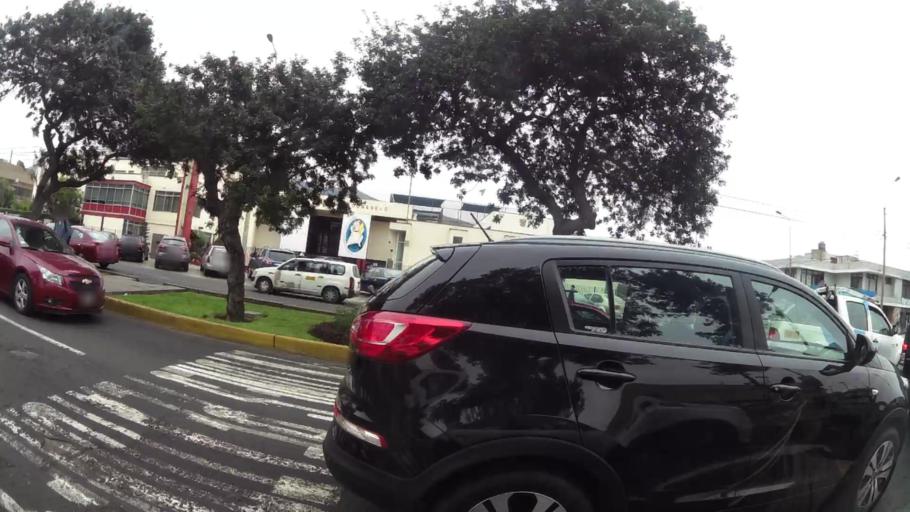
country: PE
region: Lima
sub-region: Lima
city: La Molina
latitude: -12.1094
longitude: -76.9714
